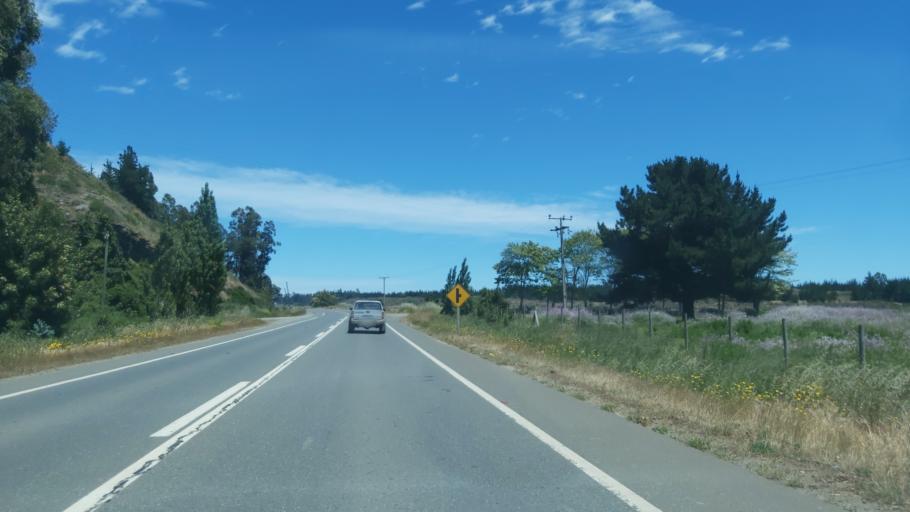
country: CL
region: Maule
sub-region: Provincia de Talca
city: Constitucion
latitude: -35.2803
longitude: -72.3569
